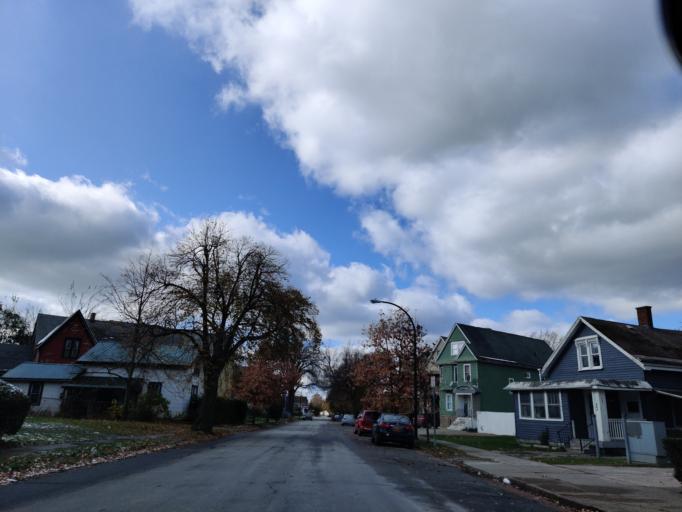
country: US
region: New York
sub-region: Erie County
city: Buffalo
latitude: 42.9113
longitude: -78.8832
